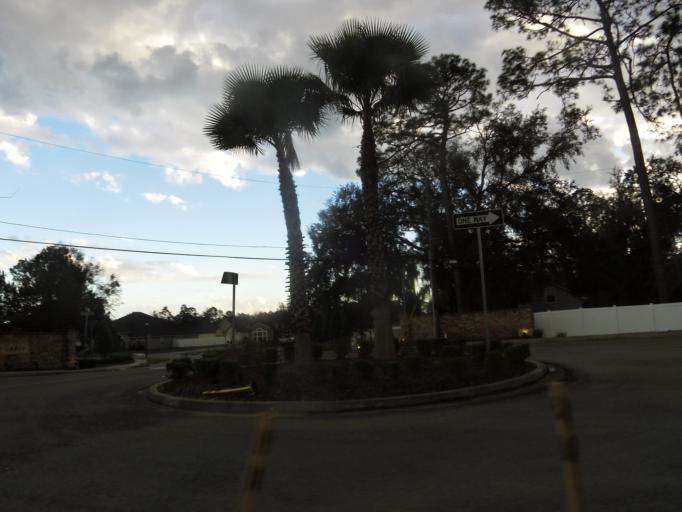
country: US
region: Florida
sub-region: Saint Johns County
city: Fruit Cove
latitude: 30.1726
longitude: -81.5686
